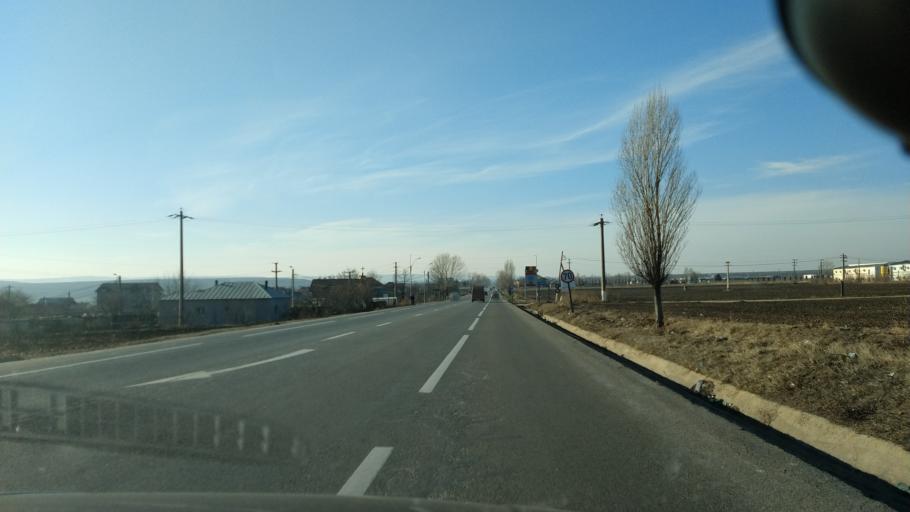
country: RO
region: Iasi
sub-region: Comuna Ion Neculce
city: Razboieni
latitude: 47.2203
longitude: 27.0708
